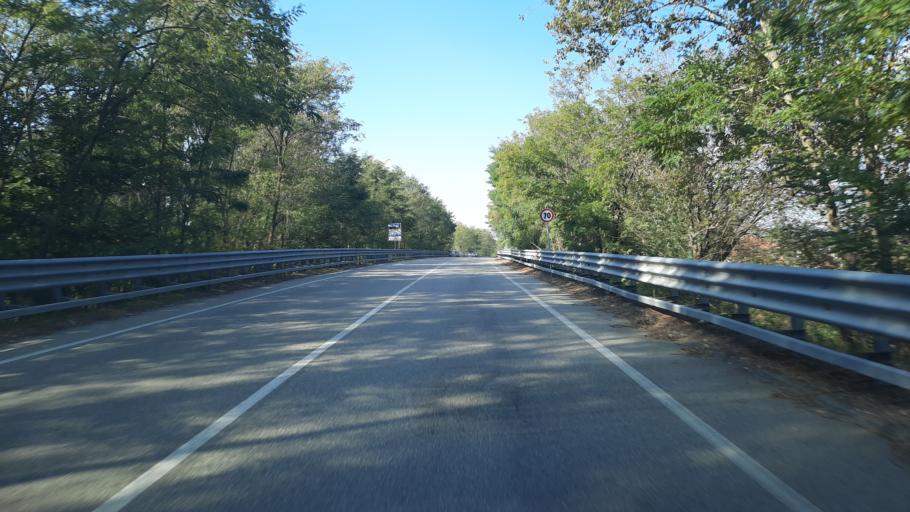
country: IT
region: Piedmont
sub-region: Provincia di Novara
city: Borgomanero
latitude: 45.6940
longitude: 8.4838
